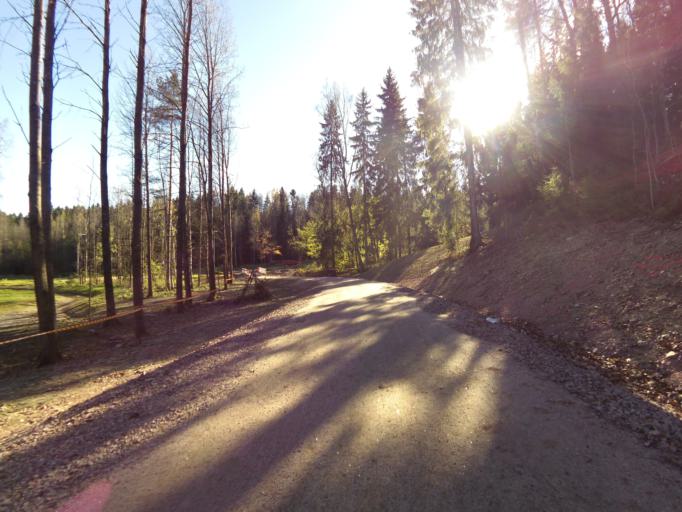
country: FI
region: Uusimaa
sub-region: Helsinki
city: Kauniainen
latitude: 60.1770
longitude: 24.7131
